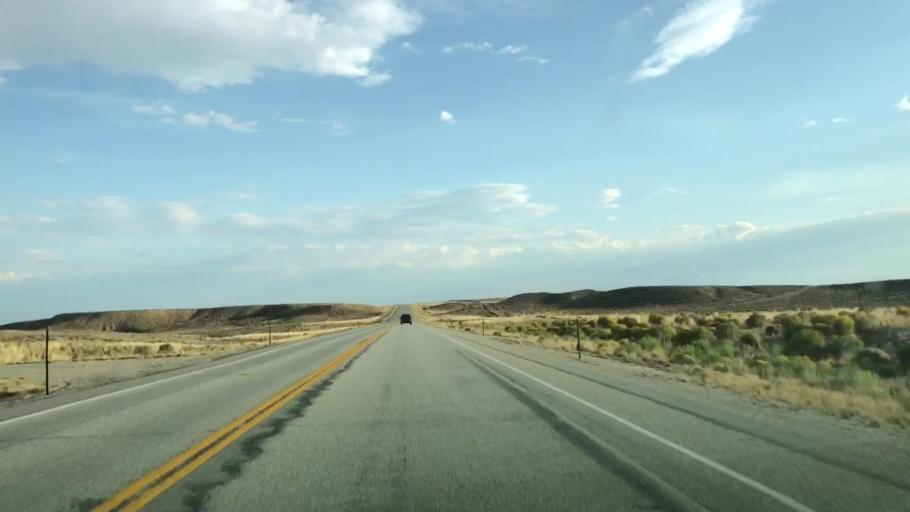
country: US
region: Wyoming
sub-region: Sublette County
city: Pinedale
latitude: 42.3496
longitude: -109.5220
